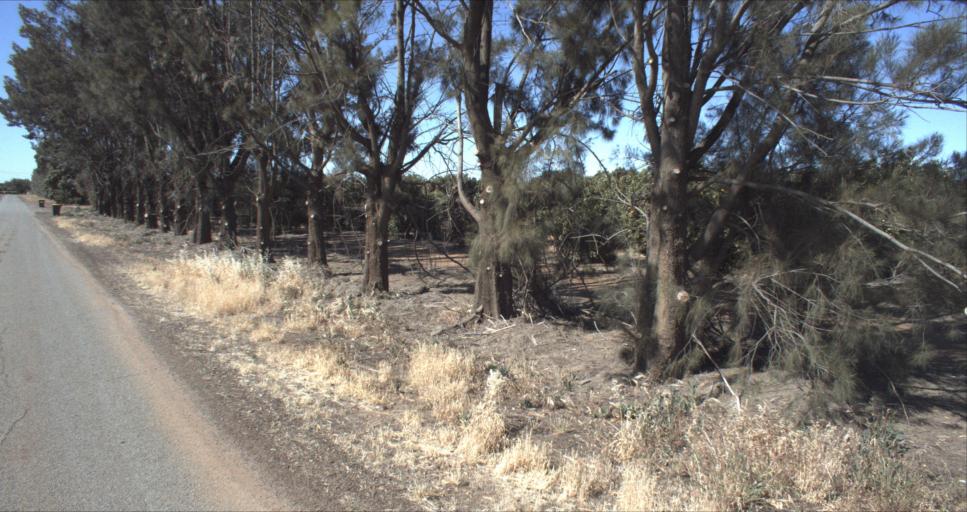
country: AU
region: New South Wales
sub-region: Leeton
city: Leeton
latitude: -34.5369
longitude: 146.3336
